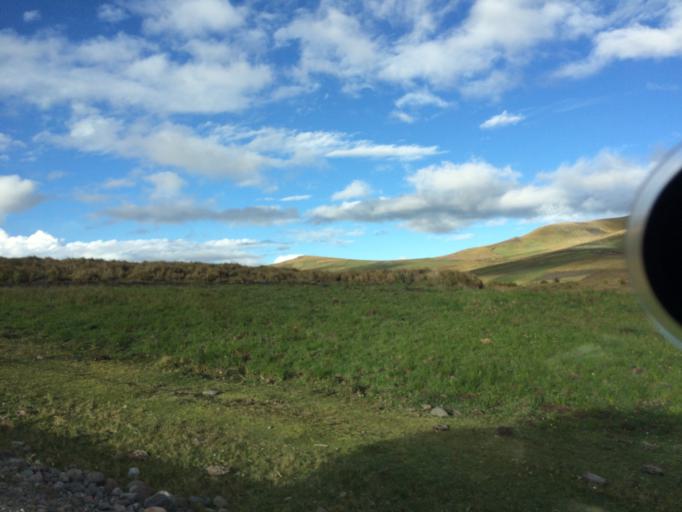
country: EC
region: Chimborazo
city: Alausi
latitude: -2.2406
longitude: -78.6819
